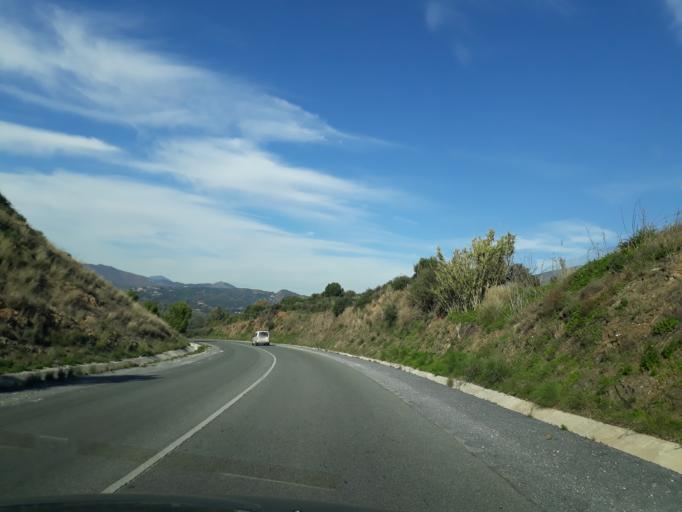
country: ES
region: Andalusia
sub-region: Provincia de Malaga
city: Fuengirola
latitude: 36.5361
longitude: -4.6860
